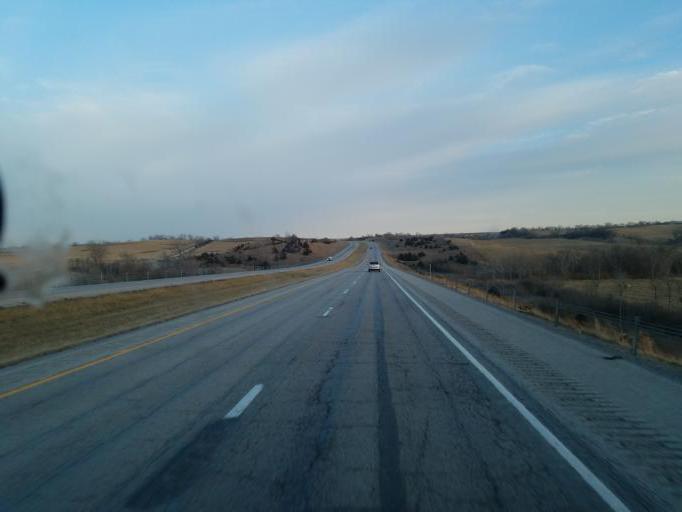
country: US
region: Iowa
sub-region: Harrison County
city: Missouri Valley
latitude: 41.4934
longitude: -95.8296
